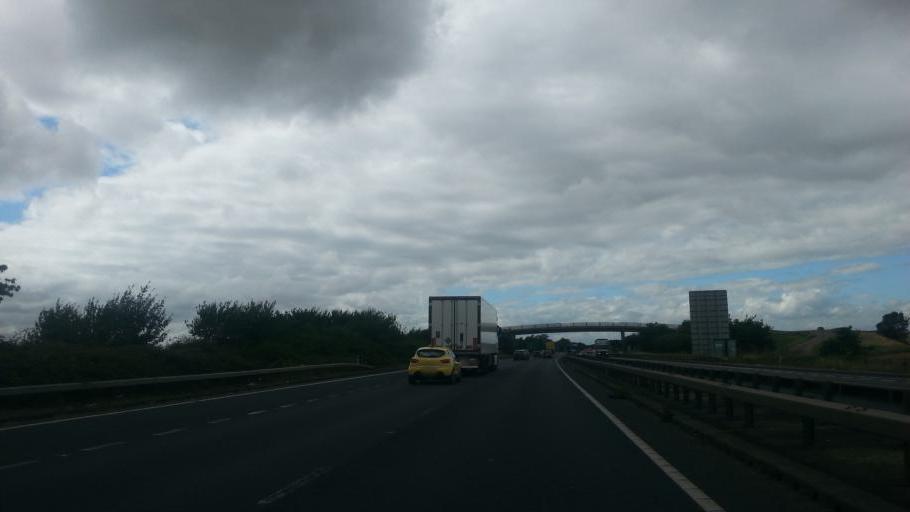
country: GB
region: England
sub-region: Cambridgeshire
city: Great Stukeley
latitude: 52.3429
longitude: -0.2131
